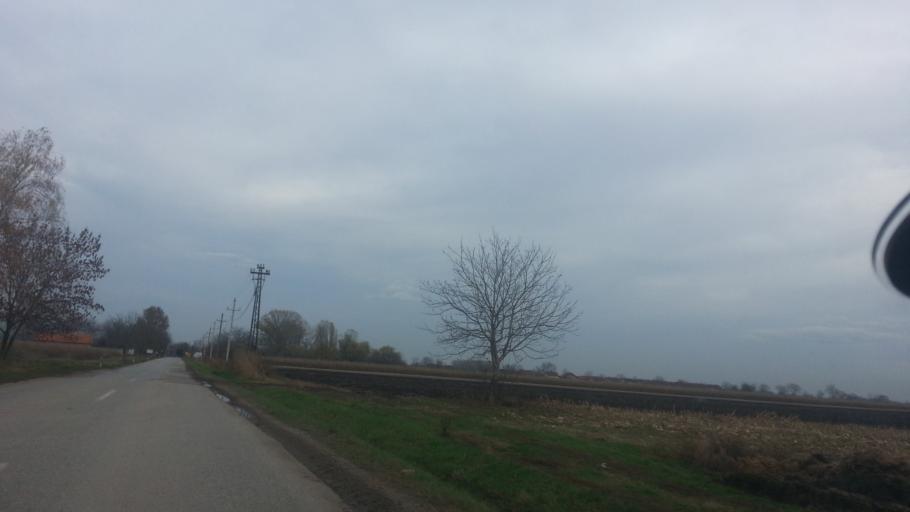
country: RS
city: Golubinci
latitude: 44.9872
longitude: 20.0391
